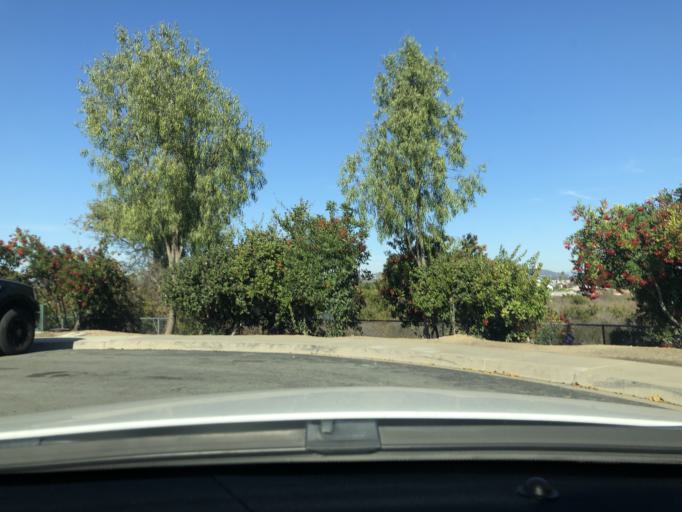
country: US
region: California
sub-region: San Diego County
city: Lemon Grove
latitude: 32.7408
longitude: -117.0627
